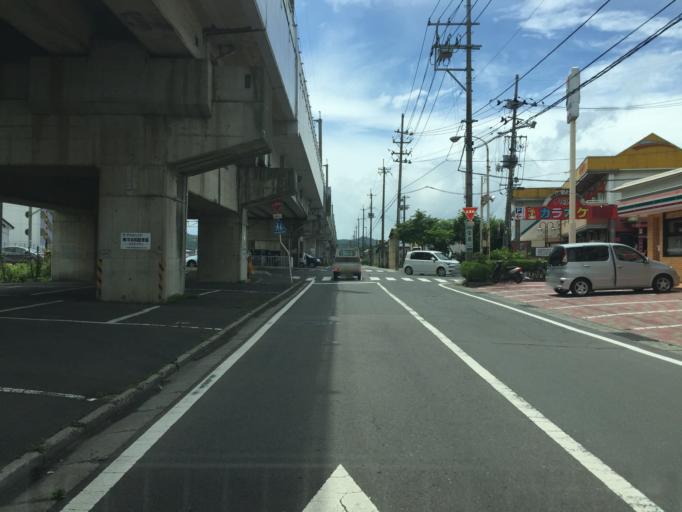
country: JP
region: Fukushima
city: Fukushima-shi
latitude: 37.7255
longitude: 140.4559
